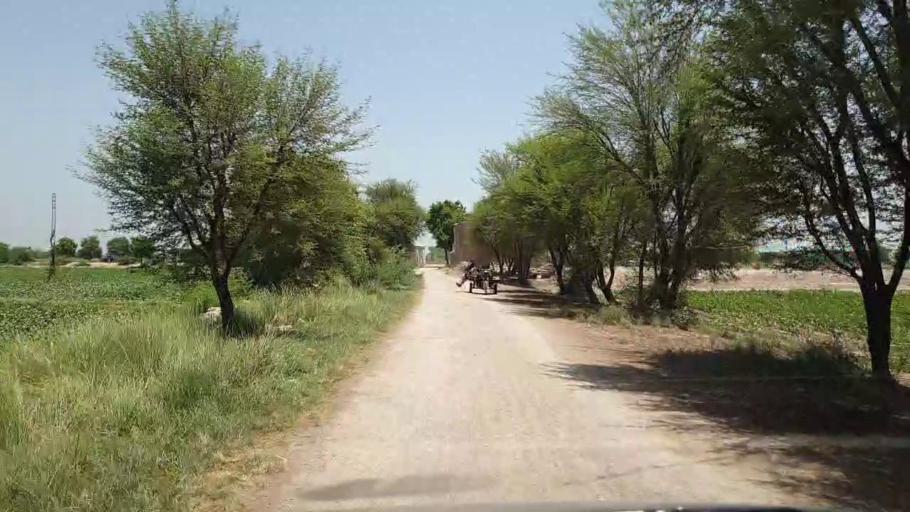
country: PK
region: Sindh
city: Sakrand
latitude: 26.1079
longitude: 68.3946
